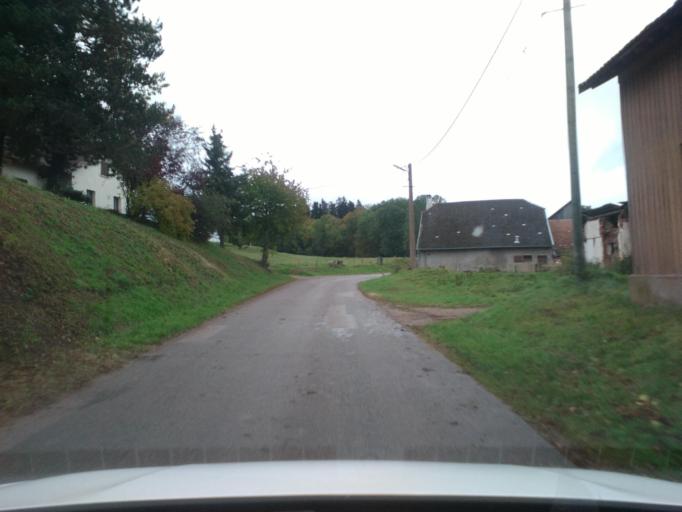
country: FR
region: Lorraine
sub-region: Departement des Vosges
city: Senones
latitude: 48.3686
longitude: 6.9601
